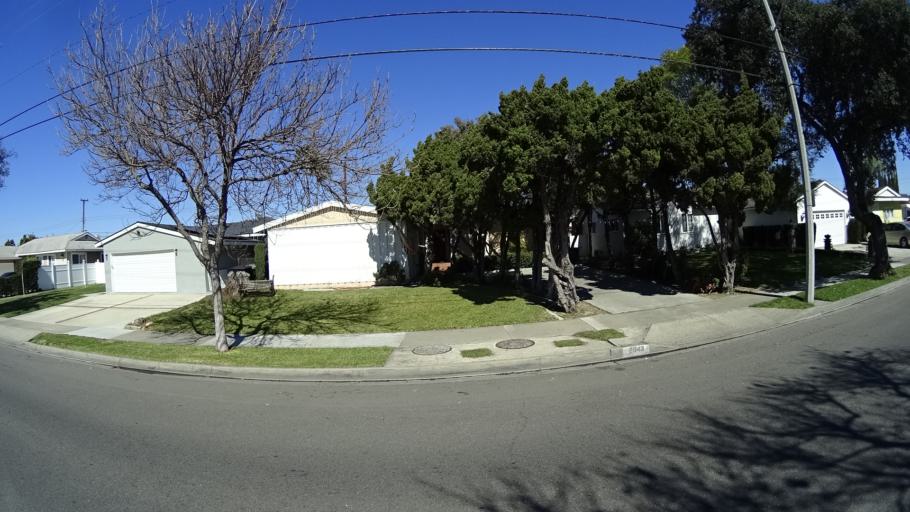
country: US
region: California
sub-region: Orange County
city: Anaheim
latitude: 33.8251
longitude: -117.9539
